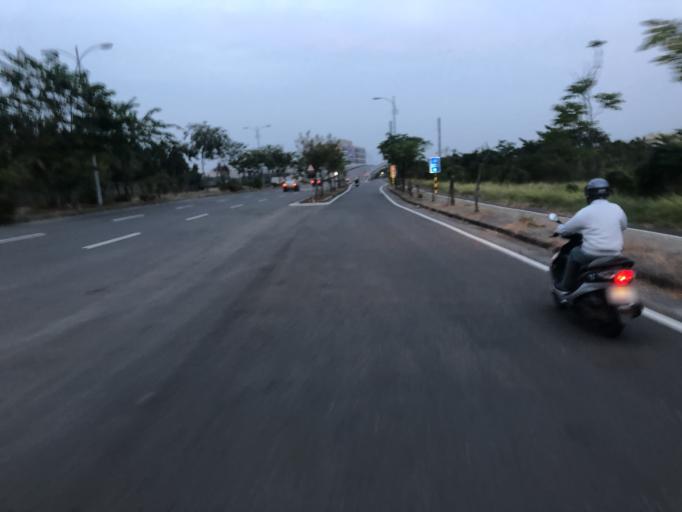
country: TW
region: Taiwan
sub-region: Tainan
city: Tainan
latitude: 23.1068
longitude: 120.2969
